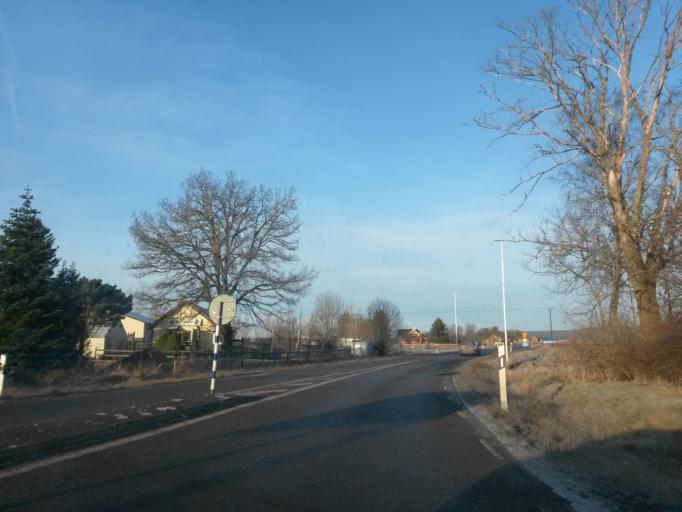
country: SE
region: Vaestra Goetaland
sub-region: Vanersborgs Kommun
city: Vargon
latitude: 58.2636
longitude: 12.4014
